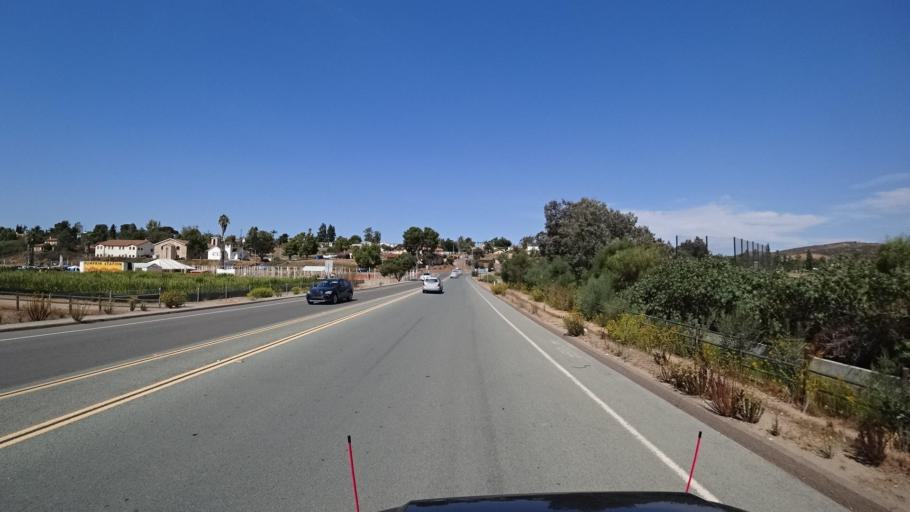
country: US
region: California
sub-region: San Diego County
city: Bonita
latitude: 32.6768
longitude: -117.0171
